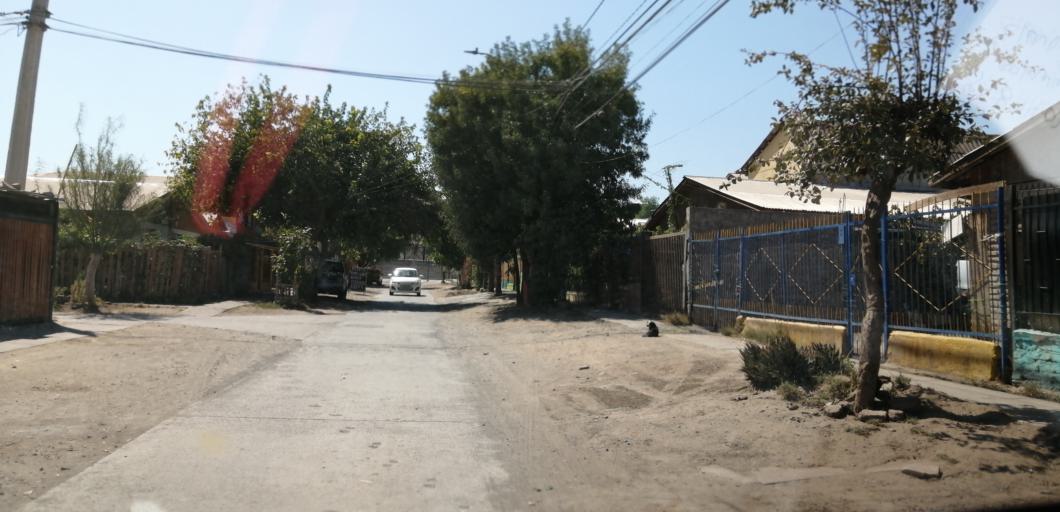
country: CL
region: Santiago Metropolitan
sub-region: Provincia de Santiago
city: Lo Prado
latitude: -33.4484
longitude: -70.7490
